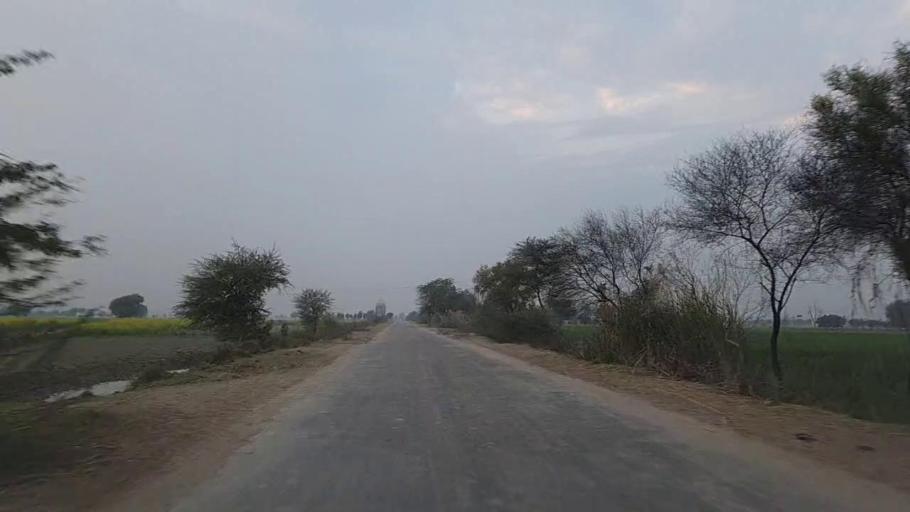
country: PK
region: Sindh
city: Jam Sahib
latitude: 26.3162
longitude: 68.5705
